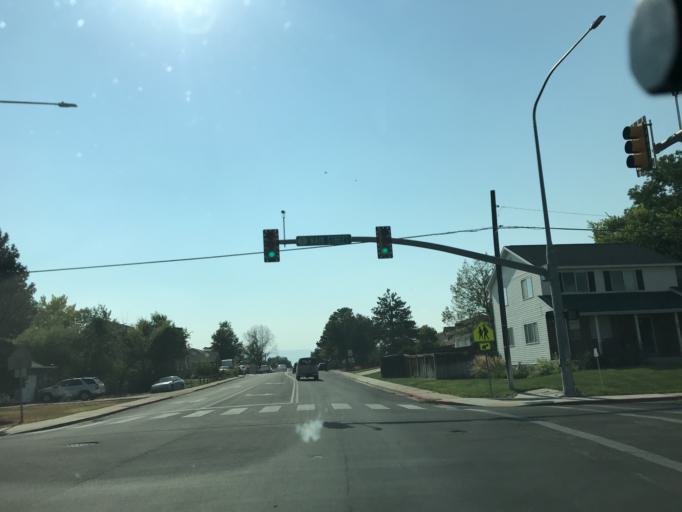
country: US
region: Utah
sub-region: Utah County
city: Orem
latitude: 40.2824
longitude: -111.6951
